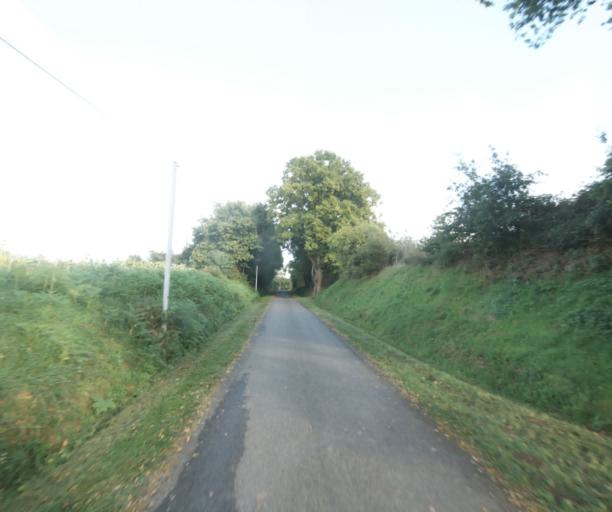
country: FR
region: Midi-Pyrenees
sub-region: Departement du Gers
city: Le Houga
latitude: 43.8426
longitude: -0.1247
